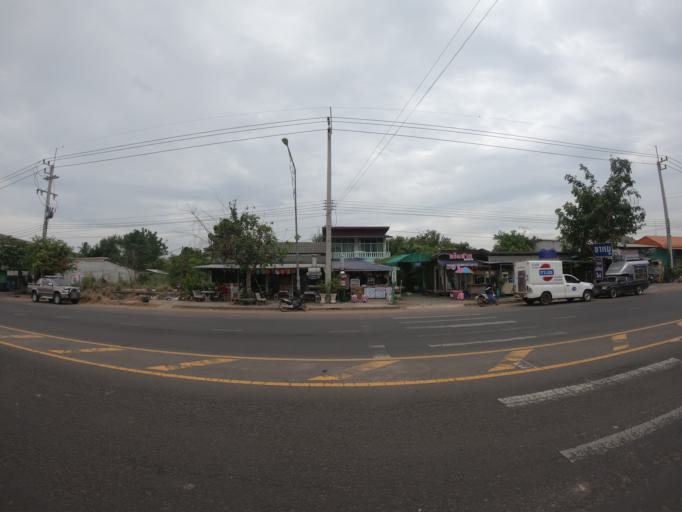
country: TH
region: Roi Et
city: Chiang Khwan
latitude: 16.1102
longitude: 103.8386
